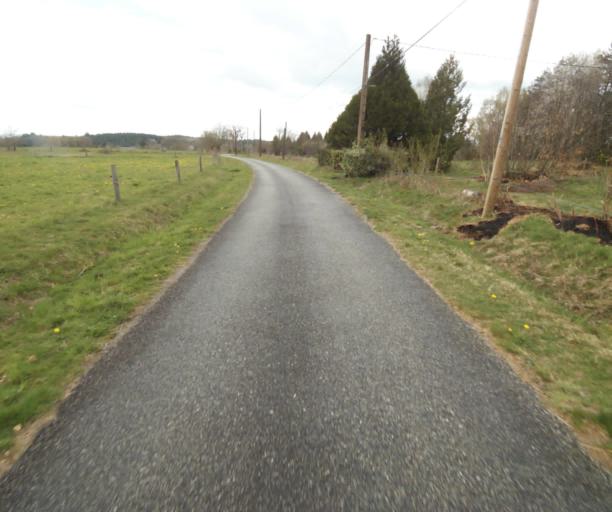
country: FR
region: Limousin
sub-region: Departement de la Correze
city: Laguenne
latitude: 45.2439
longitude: 1.8972
